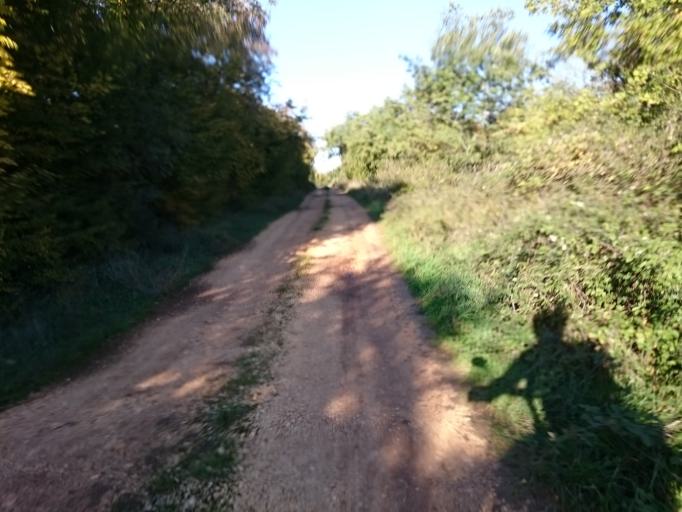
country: HR
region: Istarska
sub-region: Grad Porec
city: Porec
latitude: 45.2518
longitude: 13.6250
